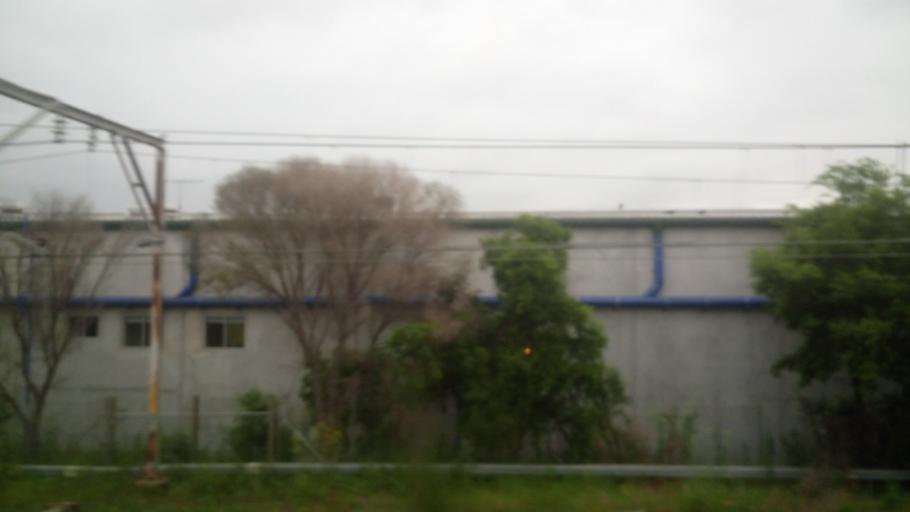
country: AU
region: New South Wales
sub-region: Strathfield
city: Homebush
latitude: -33.8647
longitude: 151.0760
